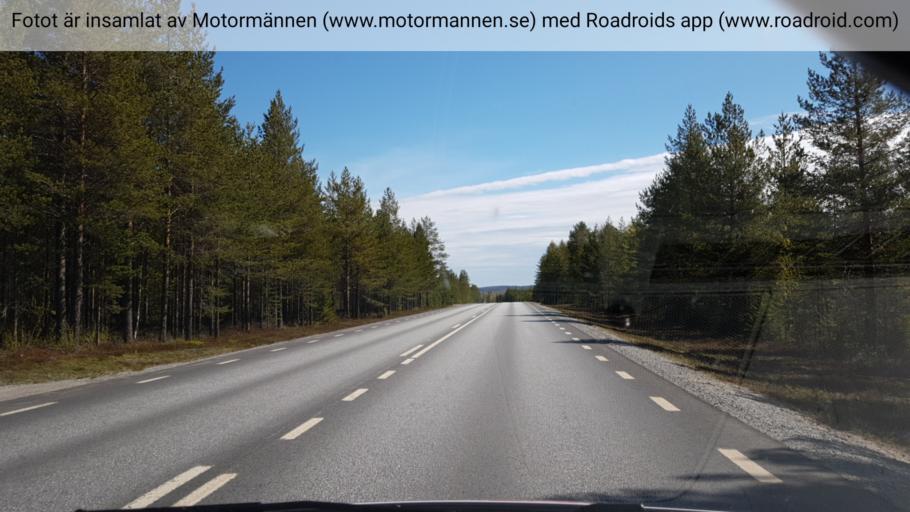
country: SE
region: Vaesterbotten
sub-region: Vannas Kommun
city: Vannasby
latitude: 64.0360
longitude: 20.0112
